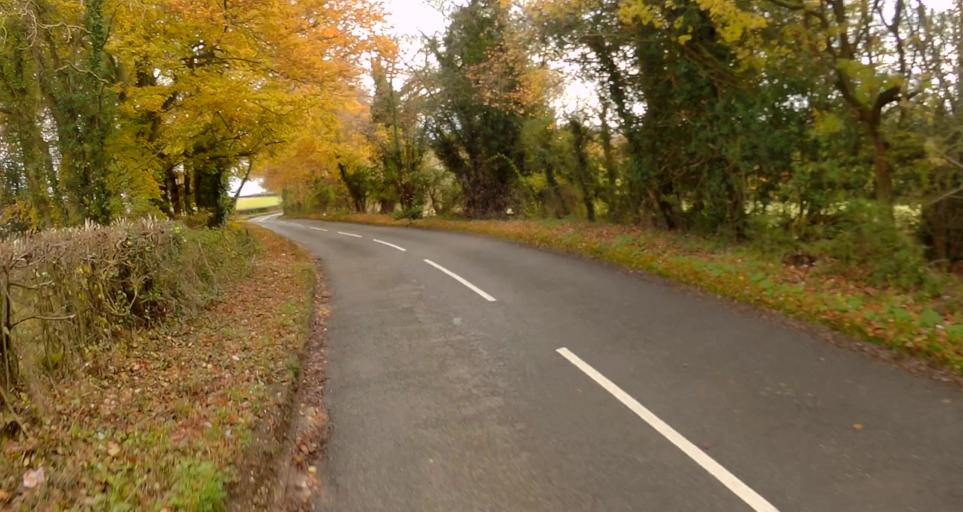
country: GB
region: England
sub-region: Hampshire
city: Old Basing
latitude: 51.2412
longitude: -1.0392
